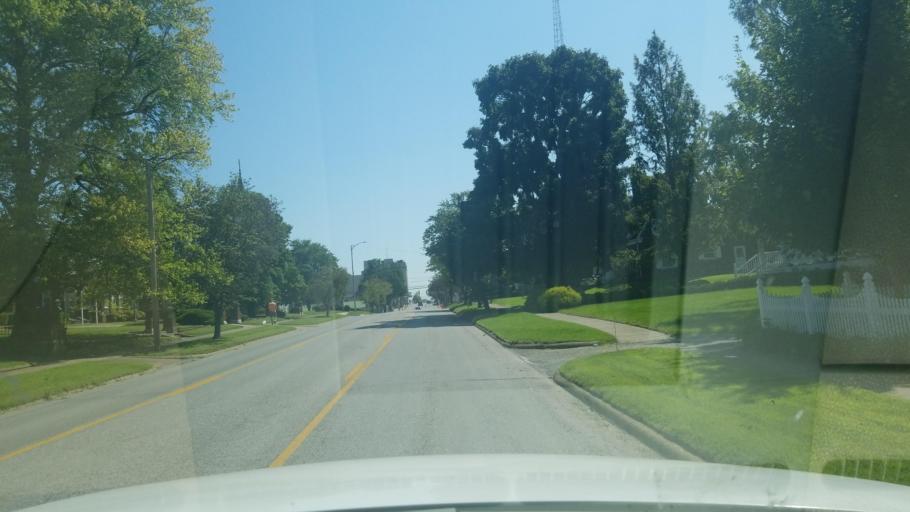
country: US
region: Illinois
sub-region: Saline County
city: Harrisburg
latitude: 37.7383
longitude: -88.5446
